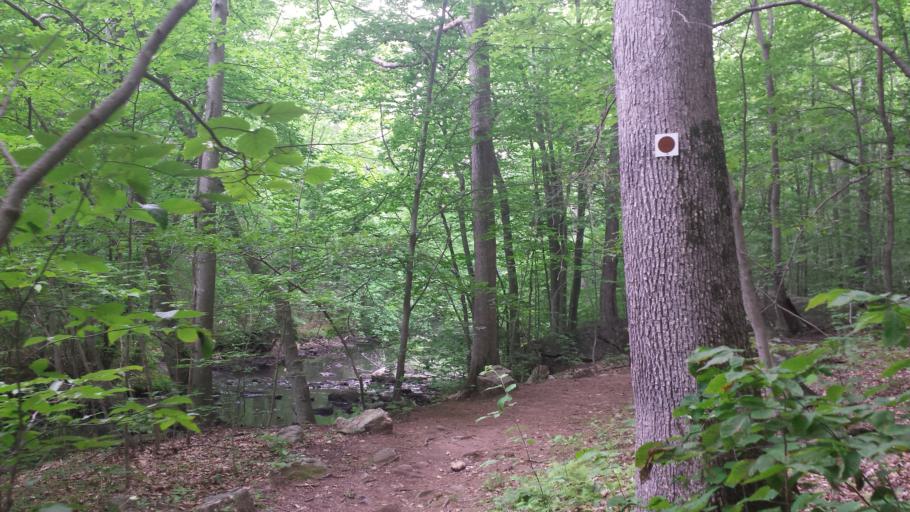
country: US
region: New York
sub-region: Westchester County
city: Pound Ridge
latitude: 41.2650
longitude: -73.5831
